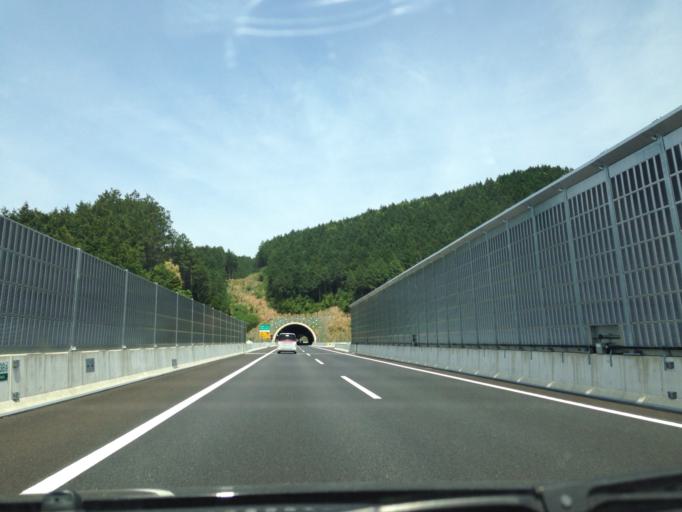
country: JP
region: Aichi
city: Okazaki
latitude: 34.9370
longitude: 137.2611
